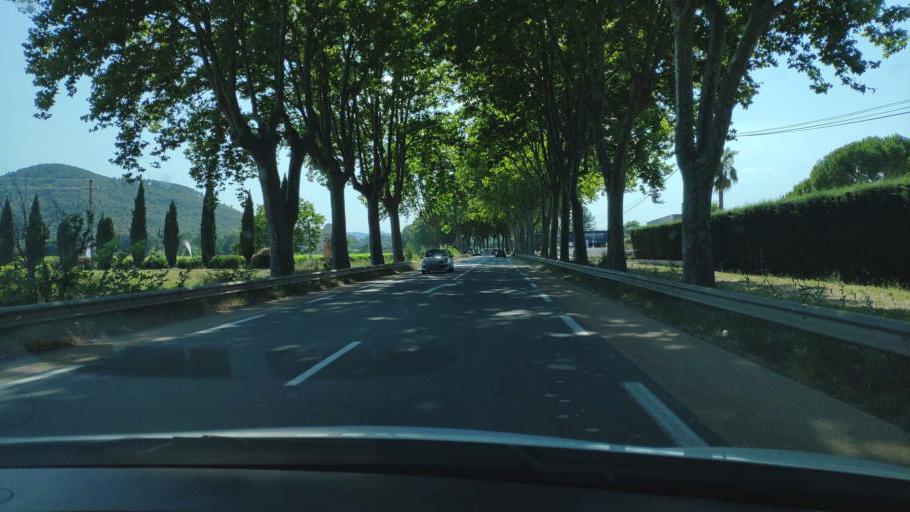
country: FR
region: Provence-Alpes-Cote d'Azur
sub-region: Departement du Var
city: Les Arcs
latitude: 43.4424
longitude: 6.4603
